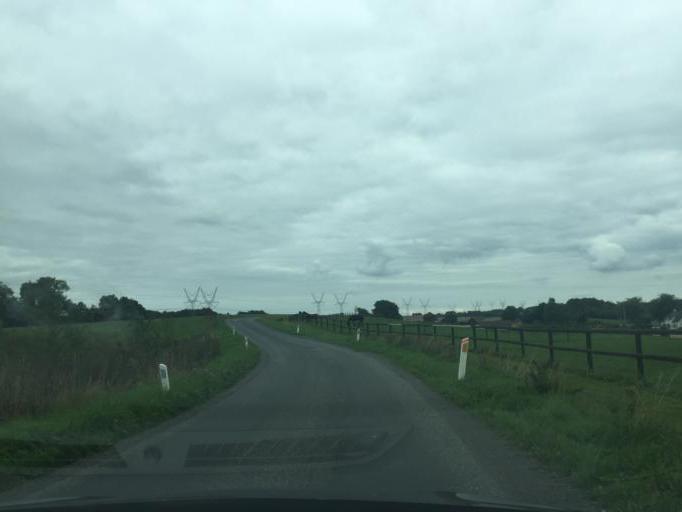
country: DK
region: South Denmark
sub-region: Assens Kommune
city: Tommerup Stationsby
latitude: 55.3795
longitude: 10.2299
